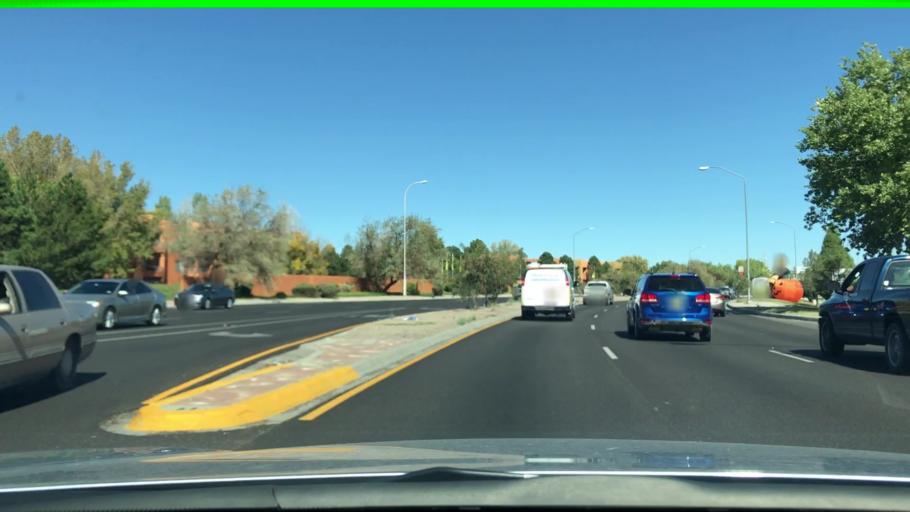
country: US
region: New Mexico
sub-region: Sandoval County
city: Rio Rancho
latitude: 35.1981
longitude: -106.6606
